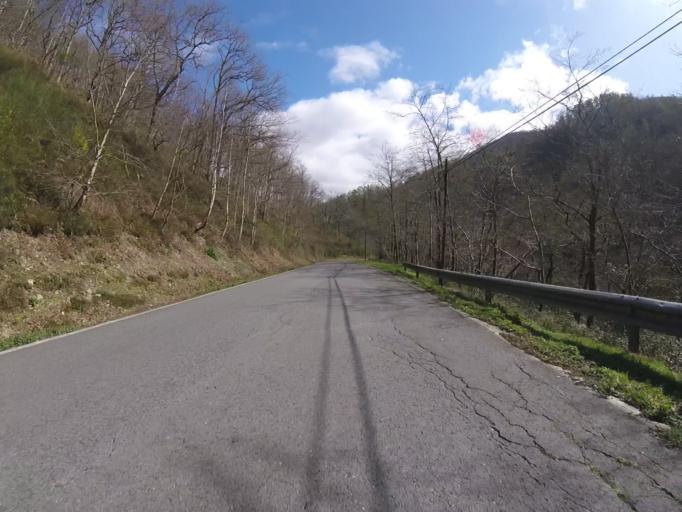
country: ES
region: Navarre
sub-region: Provincia de Navarra
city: Goizueta
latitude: 43.1375
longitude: -1.8504
